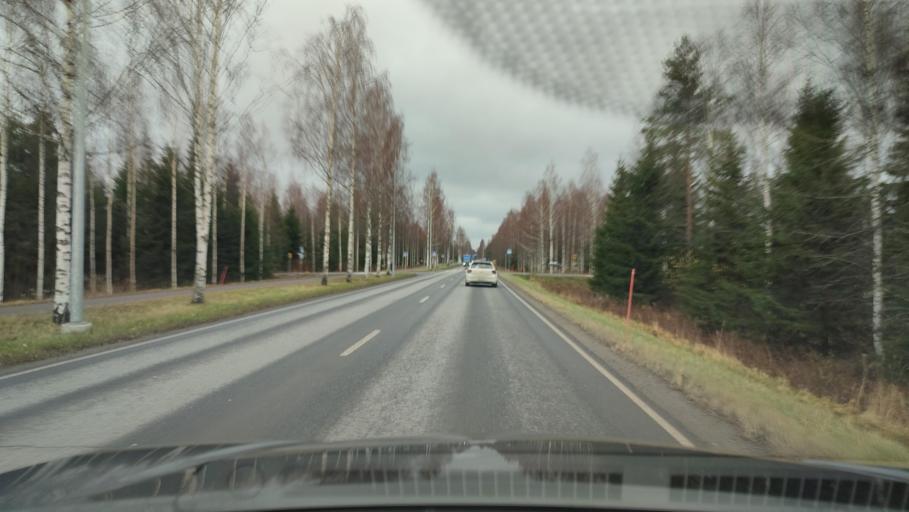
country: FI
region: Southern Ostrobothnia
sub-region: Suupohja
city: Kauhajoki
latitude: 62.4111
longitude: 22.1685
